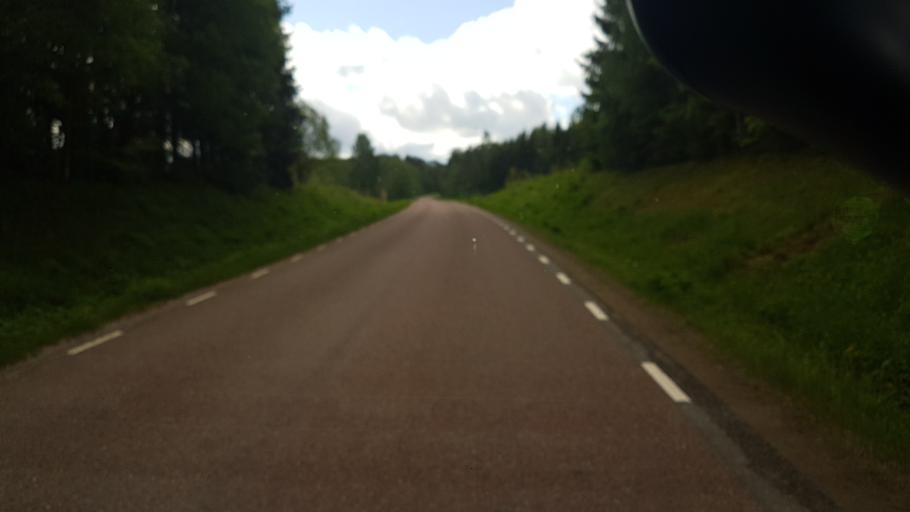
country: NO
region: Hedmark
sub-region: Eidskog
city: Skotterud
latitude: 59.7630
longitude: 12.0492
